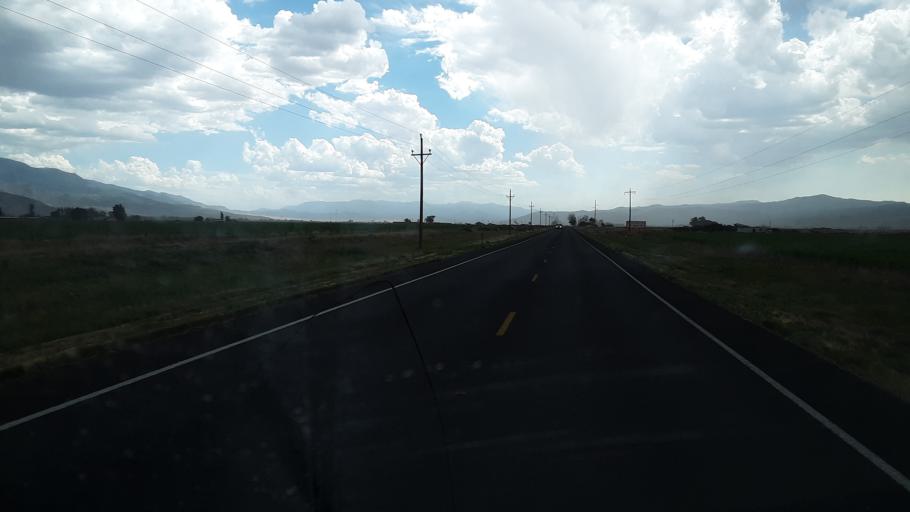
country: US
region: Utah
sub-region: Sevier County
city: Richfield
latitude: 38.8104
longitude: -112.0168
